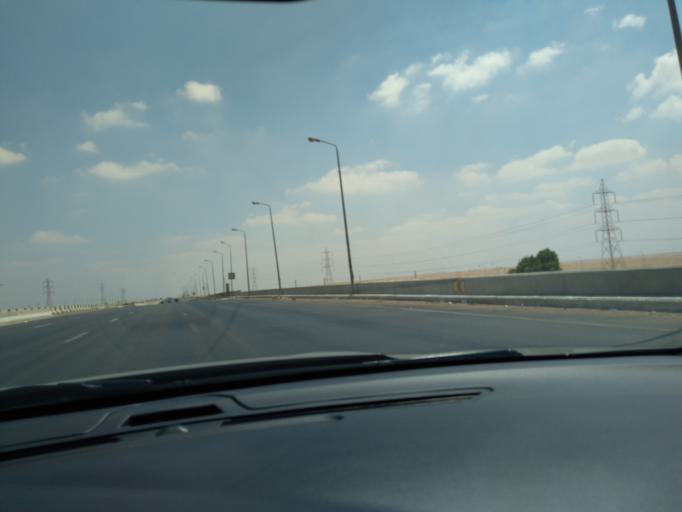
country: EG
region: Al Isma'iliyah
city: At Tall al Kabir
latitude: 30.3675
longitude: 31.9192
